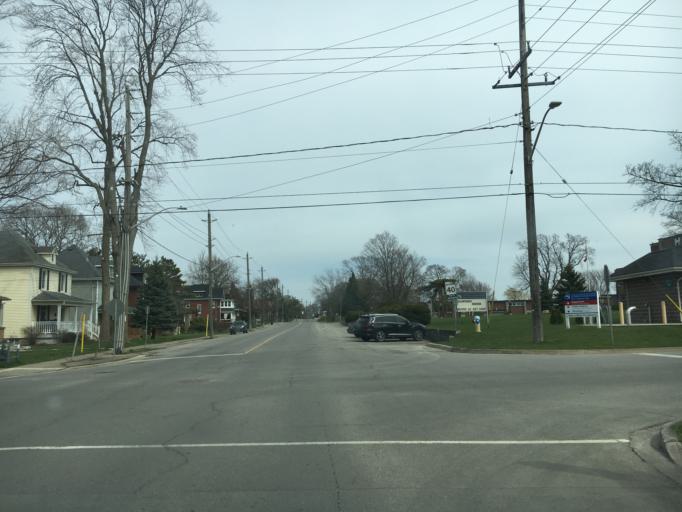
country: CA
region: Ontario
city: Port Colborne
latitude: 42.8806
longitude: -79.2602
